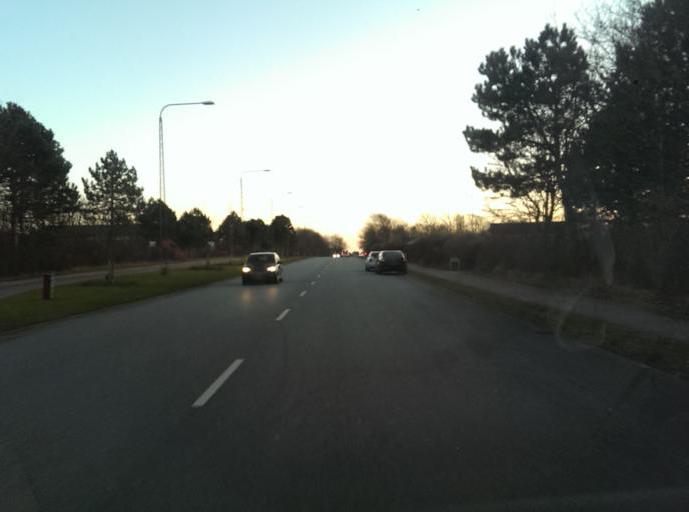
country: DK
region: South Denmark
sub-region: Esbjerg Kommune
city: Esbjerg
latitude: 55.4823
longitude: 8.4486
